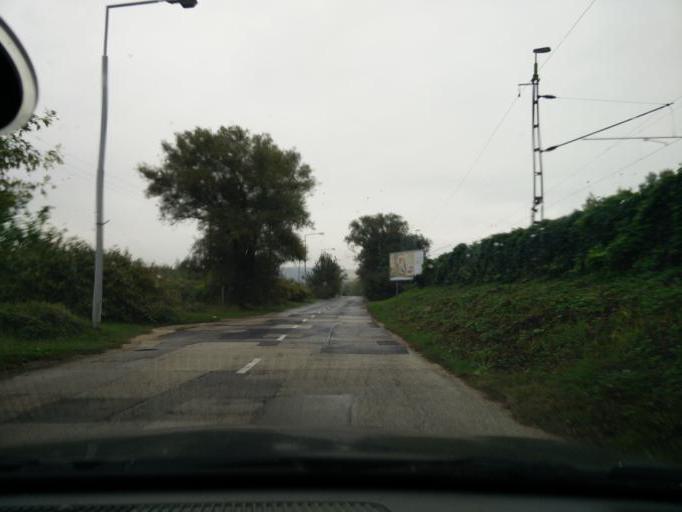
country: HU
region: Komarom-Esztergom
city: Tatabanya
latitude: 47.5635
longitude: 18.4254
